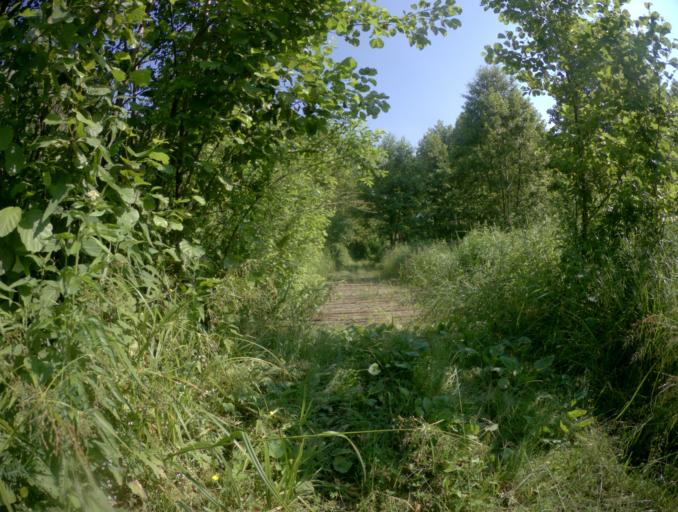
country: RU
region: Vladimir
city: Vyazniki
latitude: 56.3470
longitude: 42.1862
